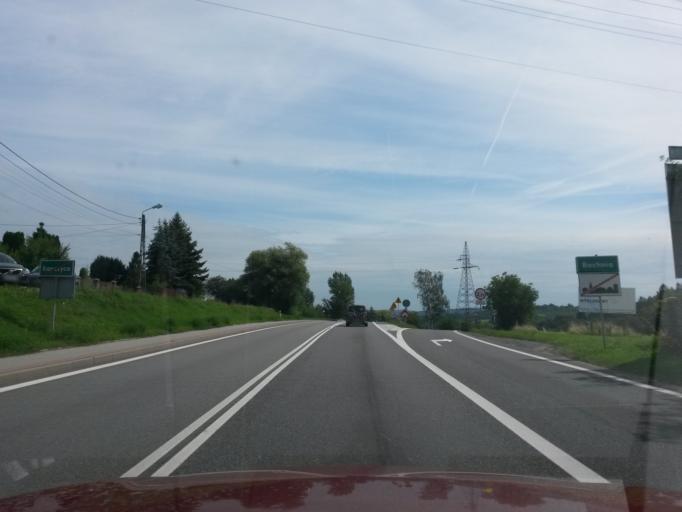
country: PL
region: Lesser Poland Voivodeship
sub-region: Powiat bochenski
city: Lapczyca
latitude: 49.9603
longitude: 20.3997
